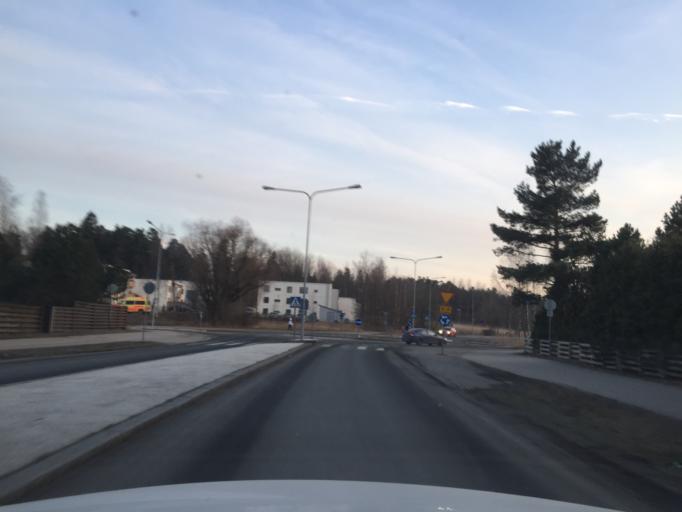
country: FI
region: Uusimaa
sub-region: Helsinki
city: Vantaa
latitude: 60.2521
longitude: 24.9820
